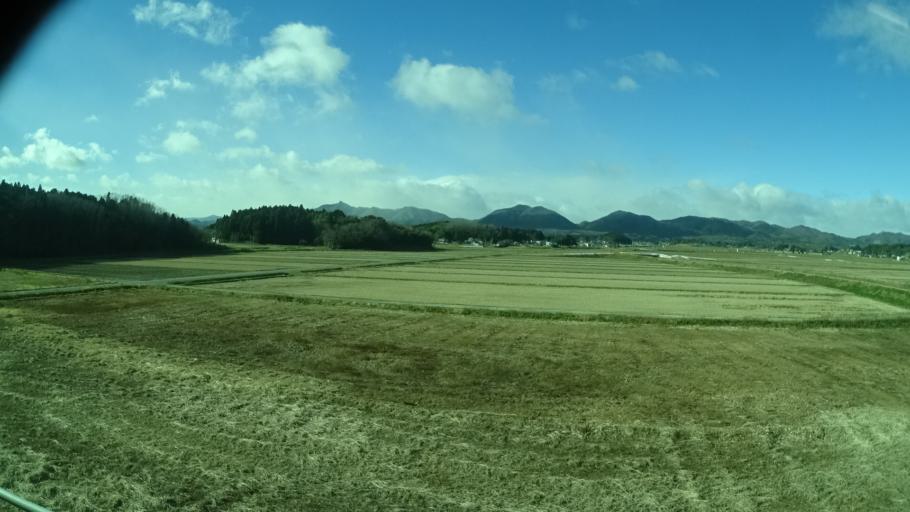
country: JP
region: Miyagi
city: Marumori
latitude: 37.8894
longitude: 140.9220
